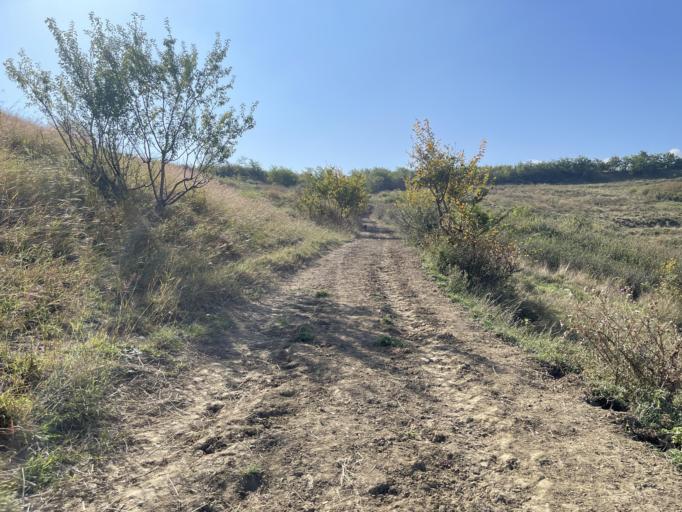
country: RO
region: Iasi
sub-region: Comuna Dumesti
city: Pausesti
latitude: 47.1592
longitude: 27.3143
